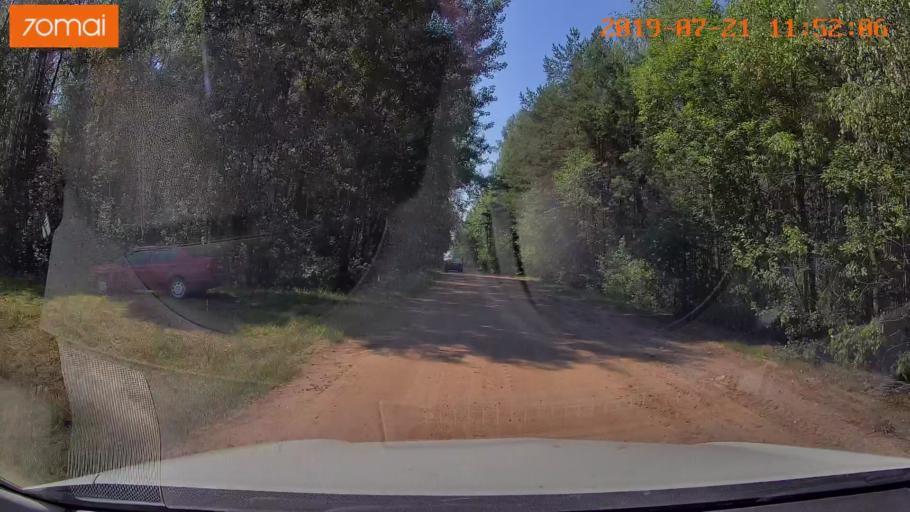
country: BY
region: Grodnenskaya
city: Lyubcha
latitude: 53.8795
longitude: 26.0091
